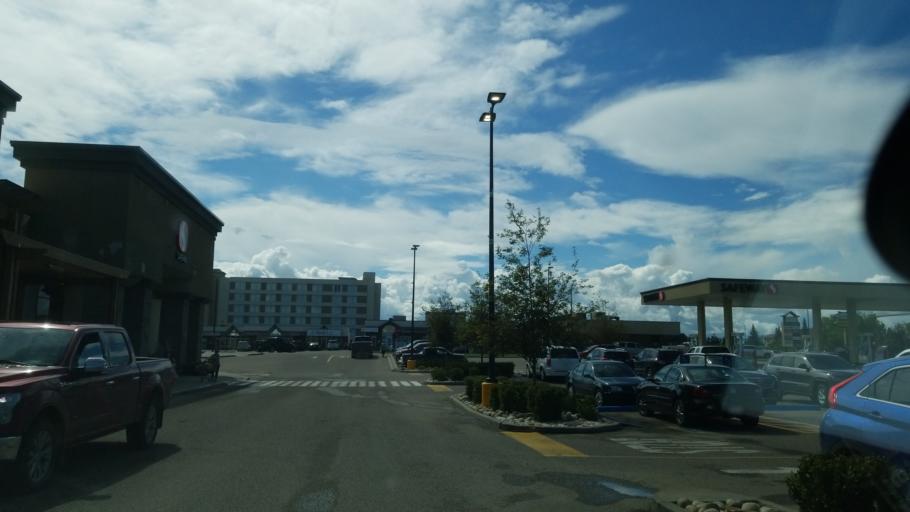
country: CA
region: Saskatchewan
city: Lloydminster
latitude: 53.2771
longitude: -110.0142
